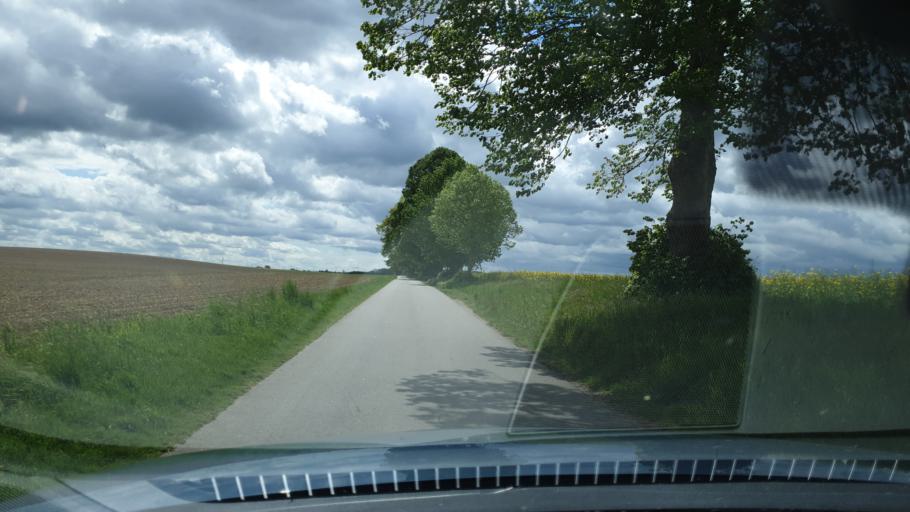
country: DE
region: Mecklenburg-Vorpommern
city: Bernitt
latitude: 53.9289
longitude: 11.8702
